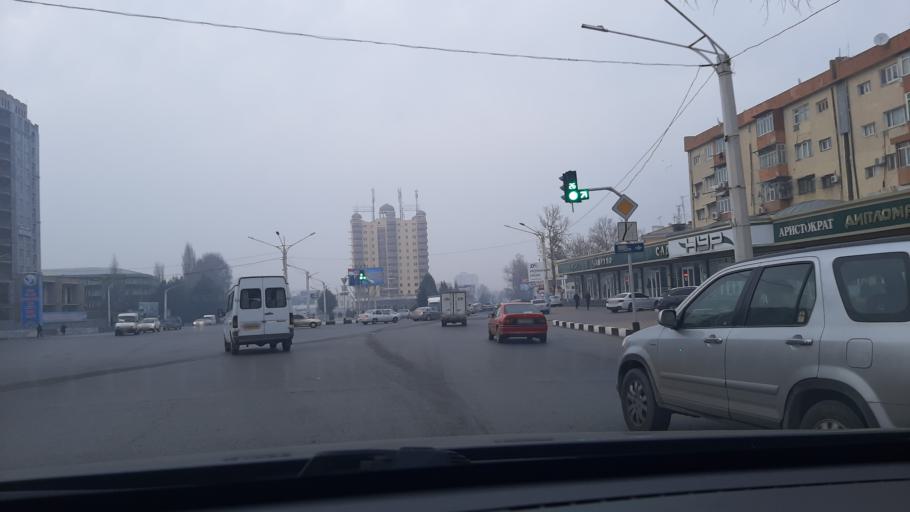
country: TJ
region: Viloyati Sughd
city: Khujand
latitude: 40.2709
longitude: 69.6446
